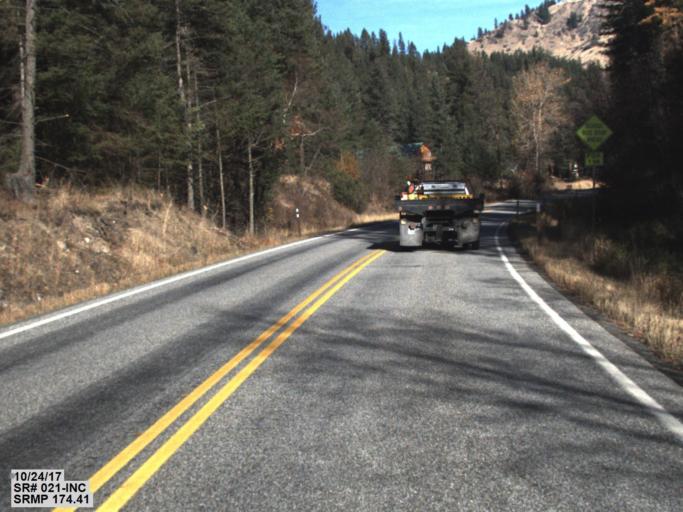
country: US
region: Washington
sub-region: Ferry County
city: Republic
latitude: 48.7939
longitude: -118.6171
